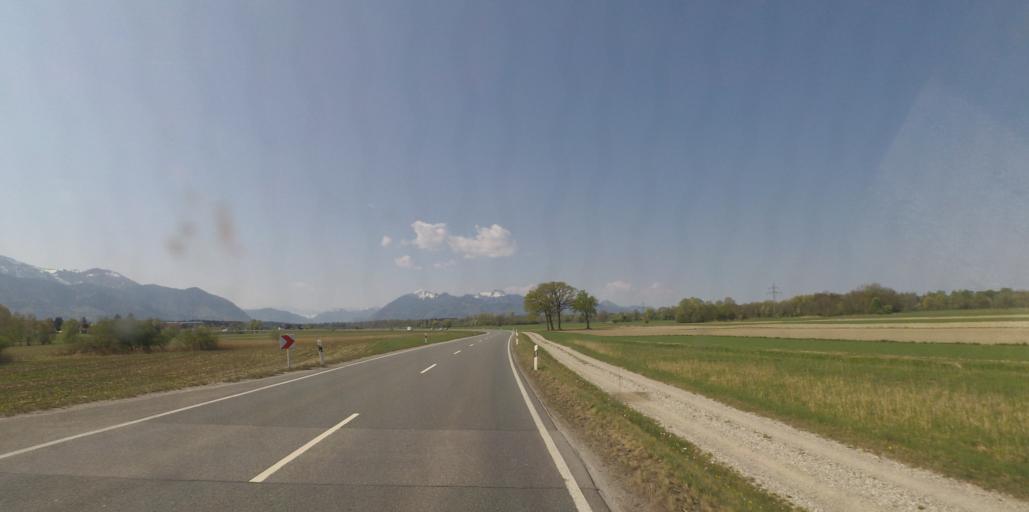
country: DE
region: Bavaria
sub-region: Upper Bavaria
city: Grabenstatt
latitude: 47.8375
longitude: 12.5282
